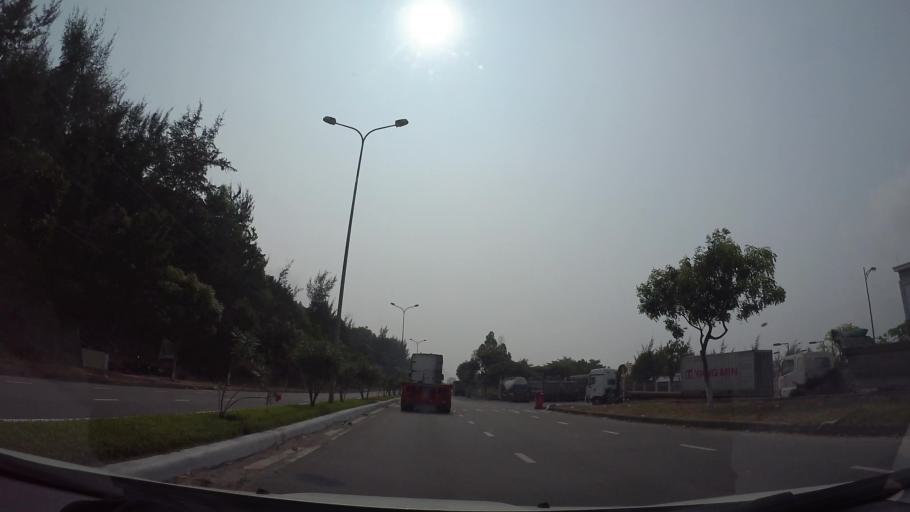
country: VN
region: Da Nang
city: Da Nang
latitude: 16.1164
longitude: 108.2325
